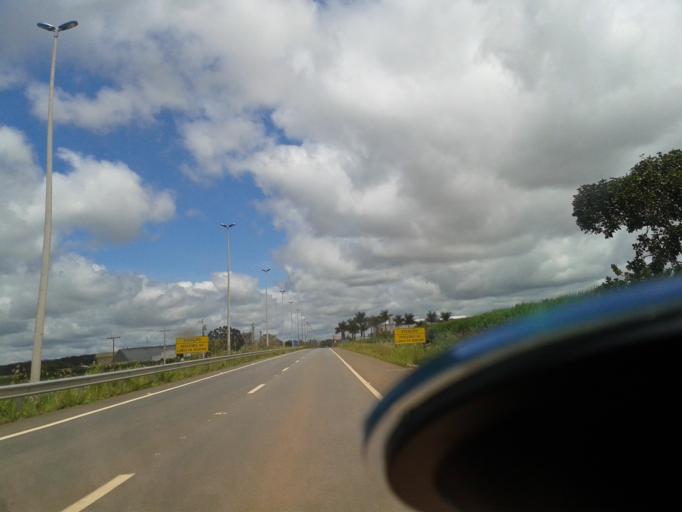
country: BR
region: Goias
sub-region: Itaberai
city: Itaberai
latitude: -16.0626
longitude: -49.7783
